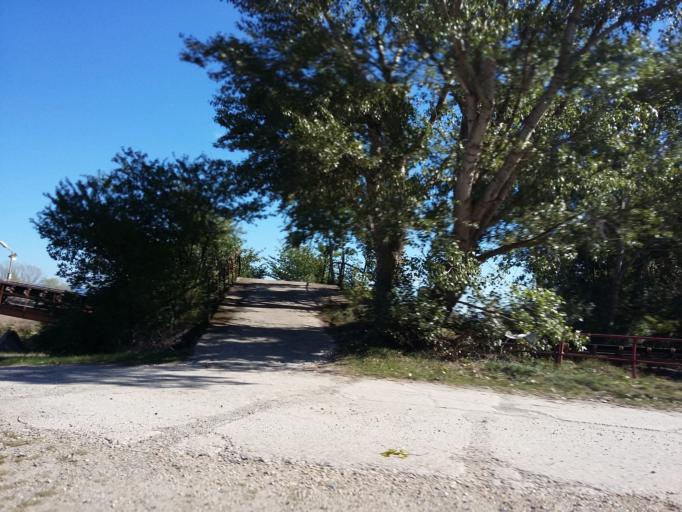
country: AT
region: Lower Austria
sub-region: Politischer Bezirk Ganserndorf
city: Marchegg
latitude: 48.3119
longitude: 16.9180
